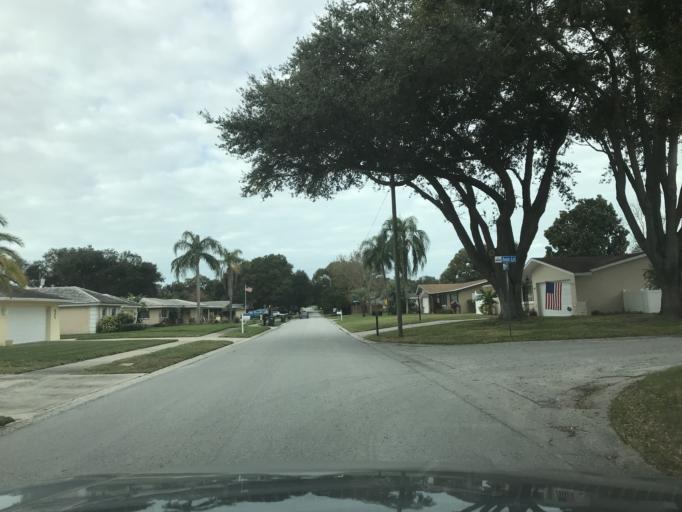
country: US
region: Florida
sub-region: Pinellas County
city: Largo
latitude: 27.9319
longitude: -82.7761
